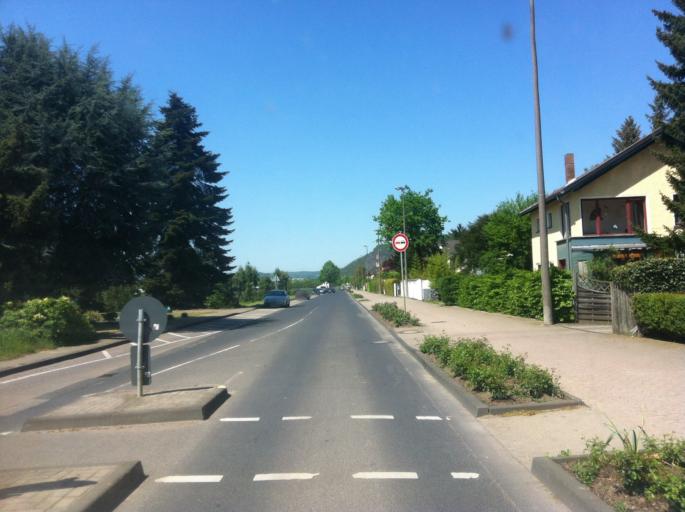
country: DE
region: Rheinland-Pfalz
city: Ockenfels
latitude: 50.5666
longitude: 7.2625
